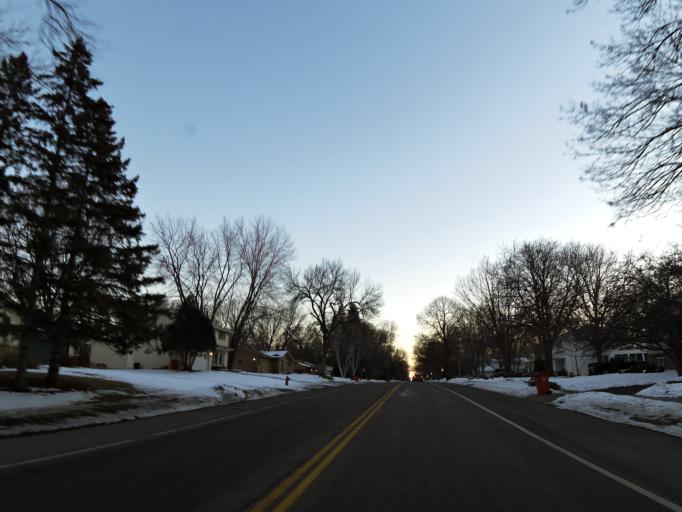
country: US
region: Minnesota
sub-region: Scott County
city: Savage
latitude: 44.8133
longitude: -93.3584
